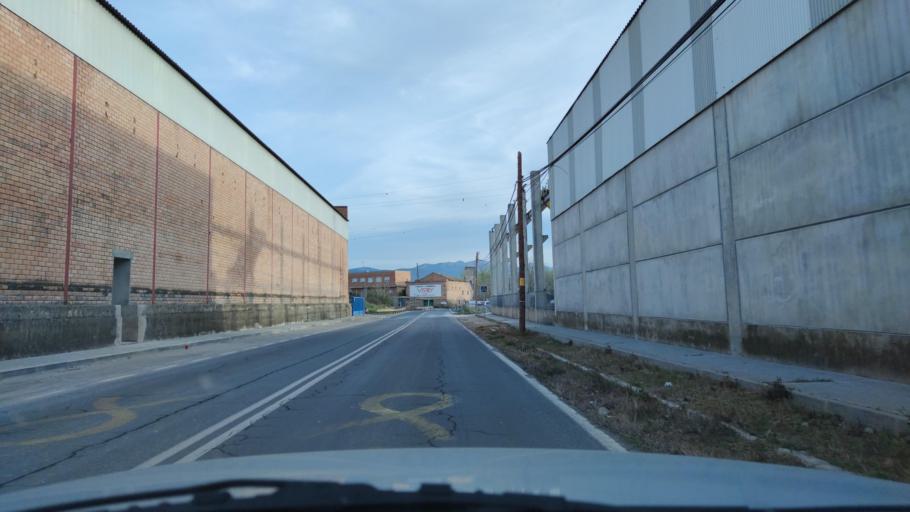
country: ES
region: Catalonia
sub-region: Provincia de Lleida
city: Balaguer
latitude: 41.8013
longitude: 0.8081
